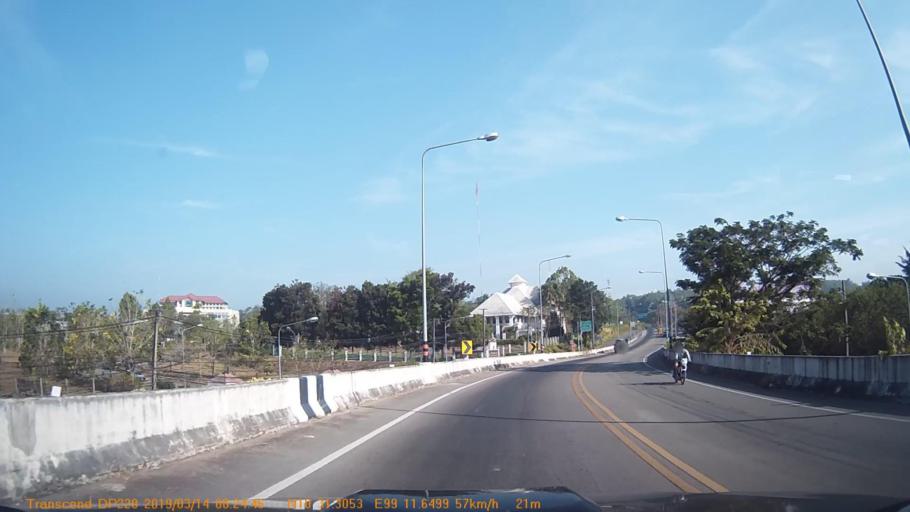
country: TH
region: Chumphon
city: Chumphon
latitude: 10.5220
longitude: 99.1940
